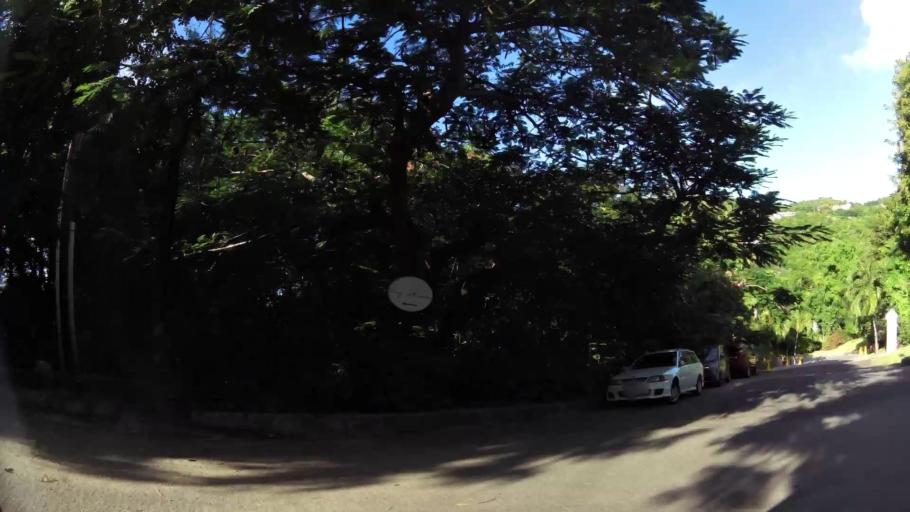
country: LC
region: Gros-Islet
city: Gros Islet
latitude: 14.1022
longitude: -60.9462
